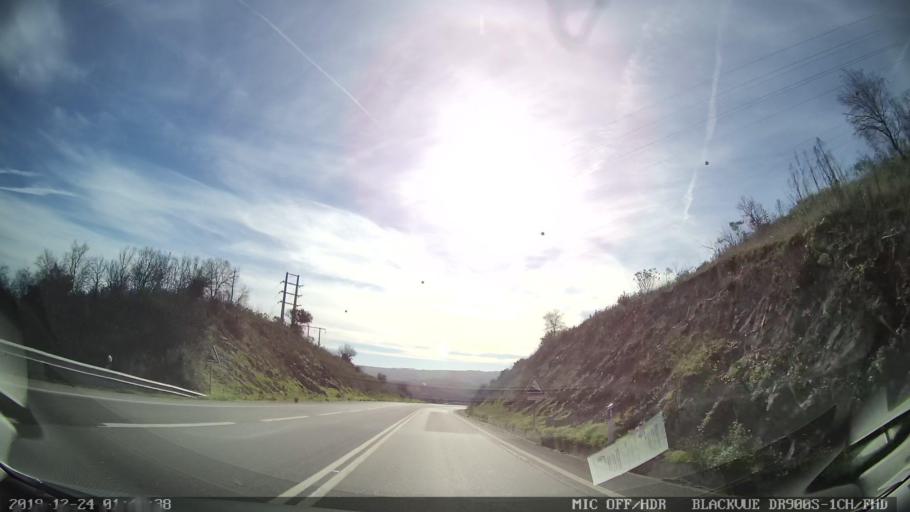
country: PT
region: Portalegre
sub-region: Nisa
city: Nisa
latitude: 39.5522
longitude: -7.7937
